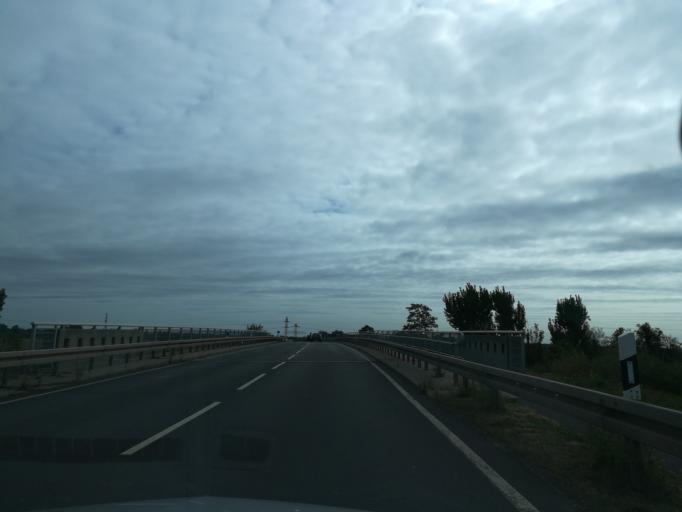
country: DE
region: Saxony-Anhalt
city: Ebendorf
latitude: 52.1783
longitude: 11.5855
